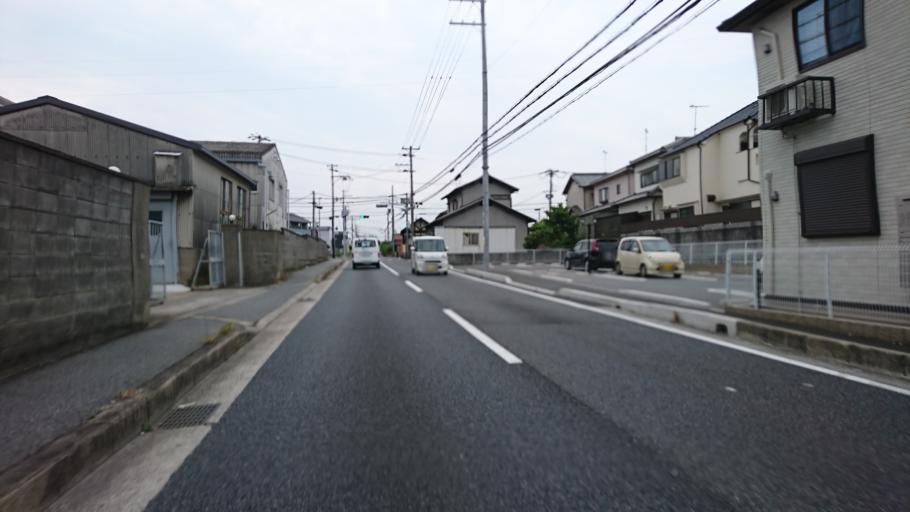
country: JP
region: Hyogo
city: Kakogawacho-honmachi
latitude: 34.7271
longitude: 134.9110
